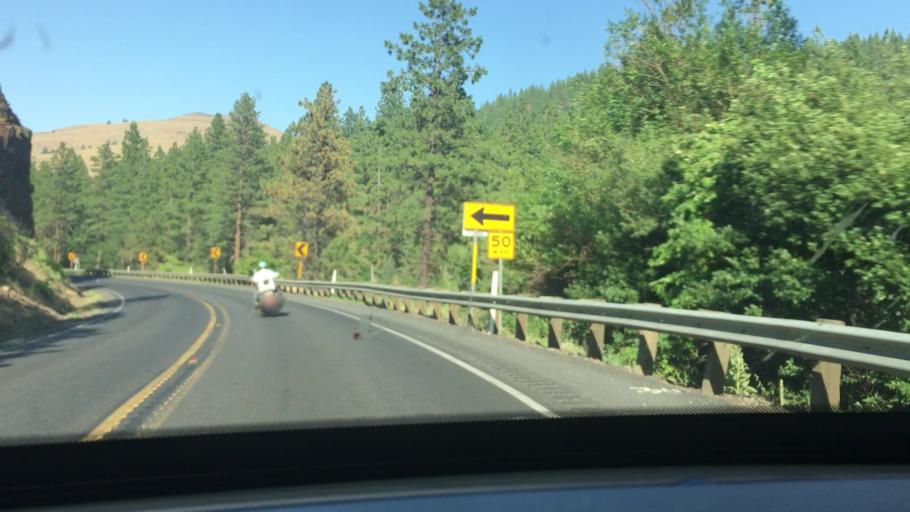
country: US
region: Washington
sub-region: Klickitat County
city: Goldendale
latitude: 46.0385
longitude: -120.5772
